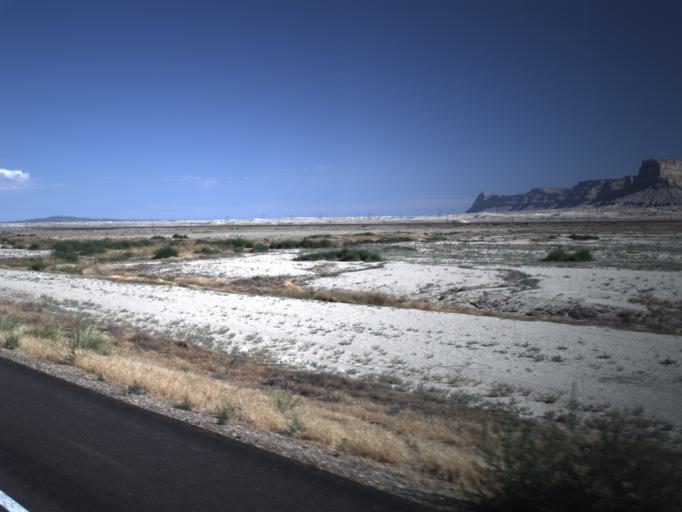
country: US
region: Utah
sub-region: Carbon County
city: East Carbon City
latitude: 38.9945
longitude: -110.2562
